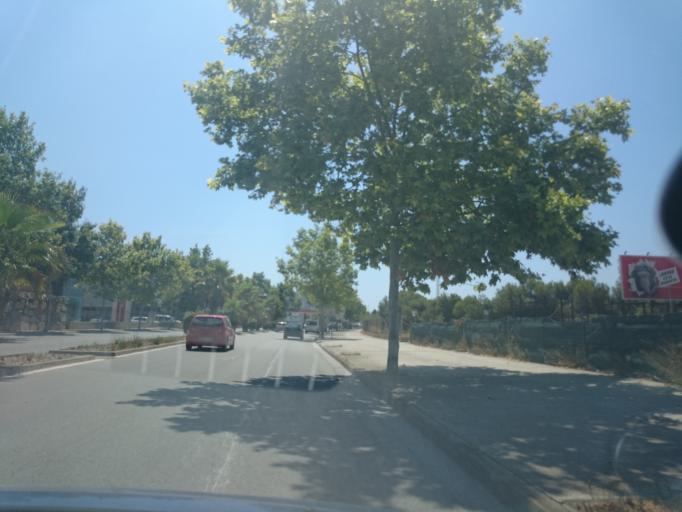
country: ES
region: Catalonia
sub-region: Provincia de Barcelona
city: Vilanova i la Geltru
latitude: 41.2335
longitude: 1.7348
